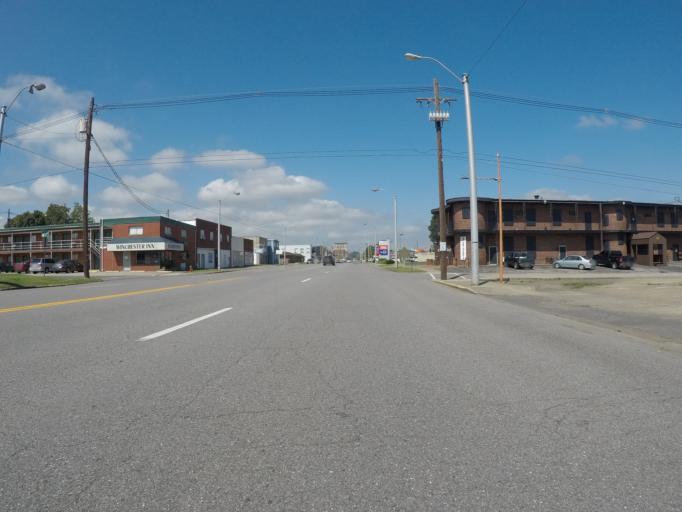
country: US
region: Kentucky
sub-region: Boyd County
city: Ashland
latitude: 38.4740
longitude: -82.6302
